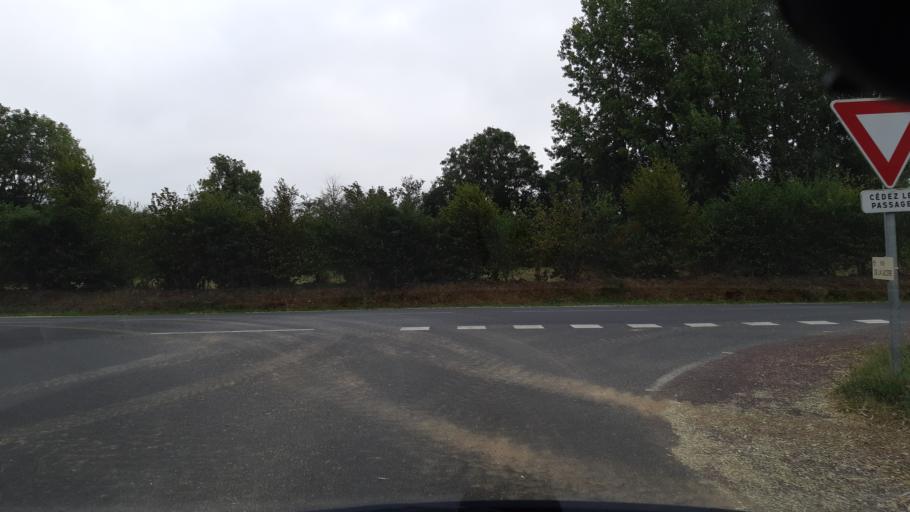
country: FR
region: Lower Normandy
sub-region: Departement de la Manche
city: Donville-les-Bains
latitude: 48.8427
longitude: -1.5541
